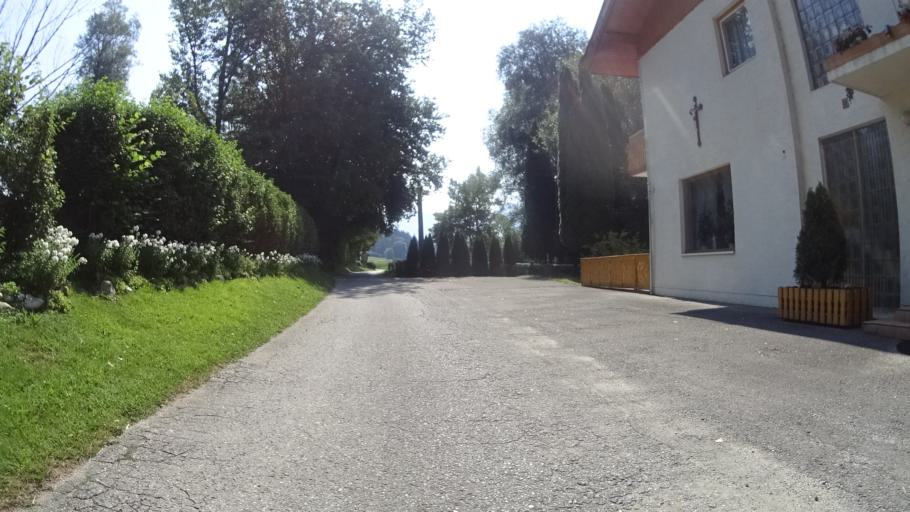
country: AT
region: Carinthia
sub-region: Politischer Bezirk Volkermarkt
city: Gallizien
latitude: 46.5639
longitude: 14.5389
